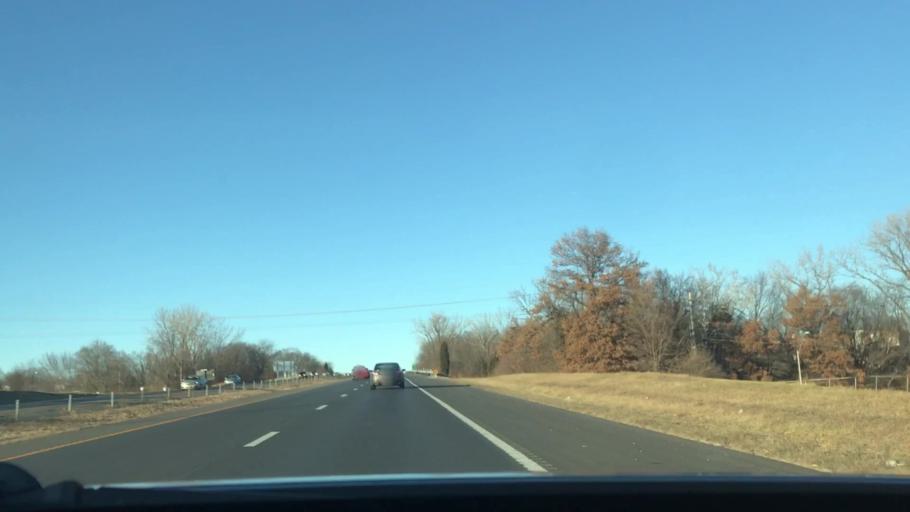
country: US
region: Missouri
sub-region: Platte County
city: Riverside
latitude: 39.2023
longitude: -94.5897
